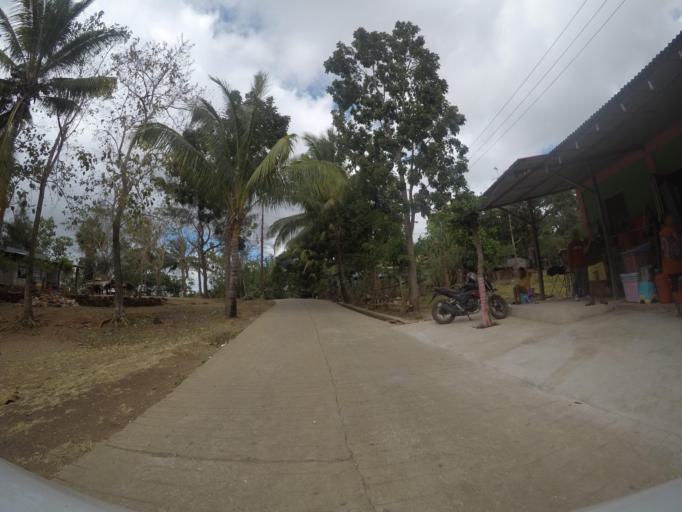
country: TL
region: Lautem
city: Lospalos
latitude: -8.5438
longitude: 126.8303
